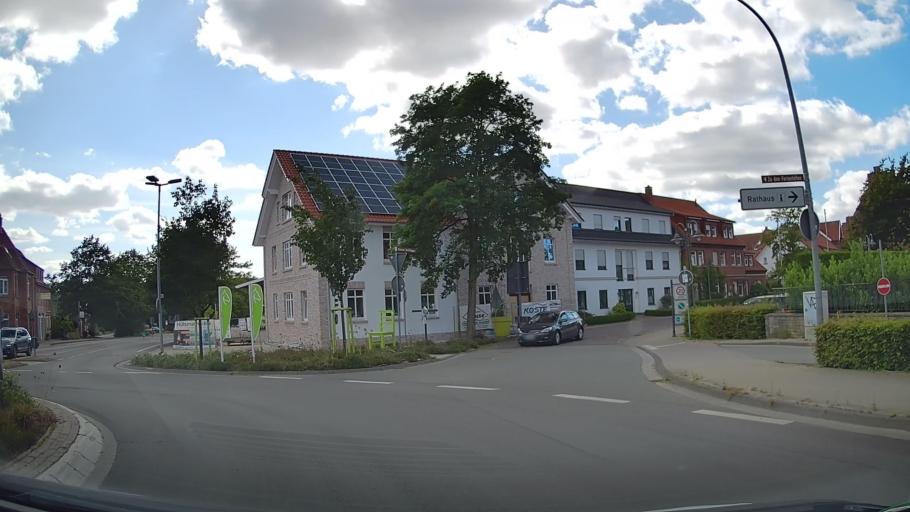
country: DE
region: Lower Saxony
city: Ankum
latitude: 52.5413
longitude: 7.8713
